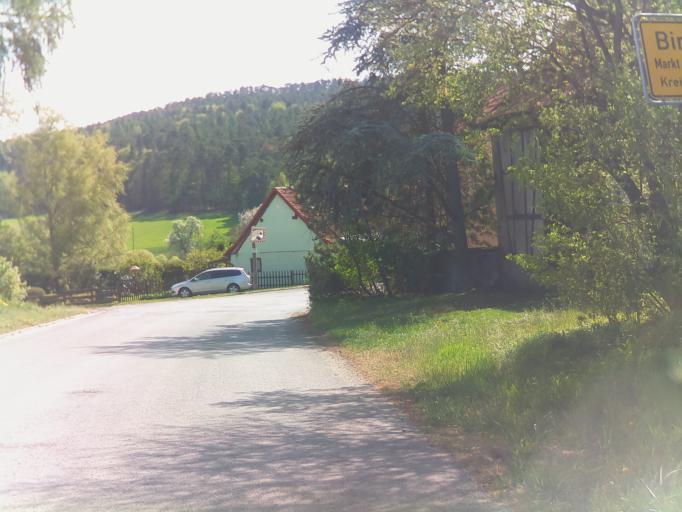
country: DE
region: Bavaria
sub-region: Regierungsbezirk Unterfranken
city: Burgpreppach
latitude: 50.1537
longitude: 10.6352
